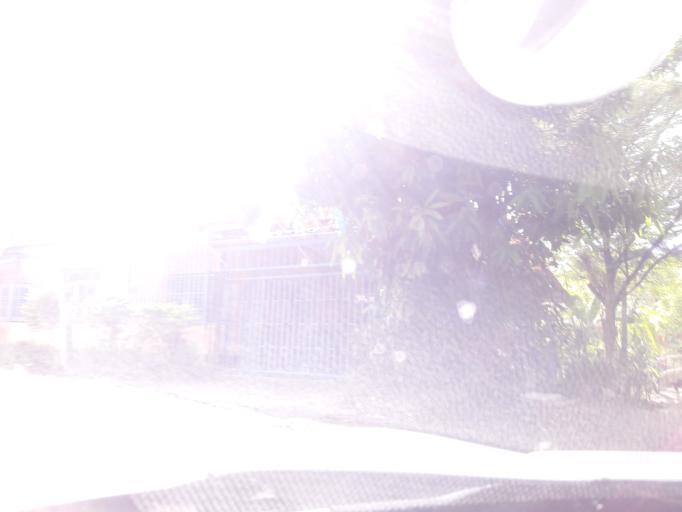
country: TH
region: Lop Buri
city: Ban Mi
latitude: 15.0437
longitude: 100.5347
